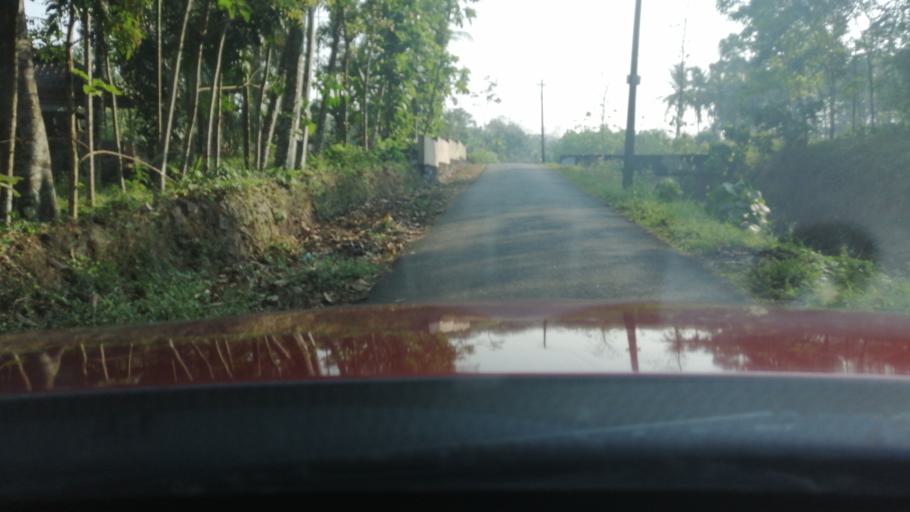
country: IN
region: Kerala
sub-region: Ernakulam
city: Piravam
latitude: 9.8941
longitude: 76.4441
